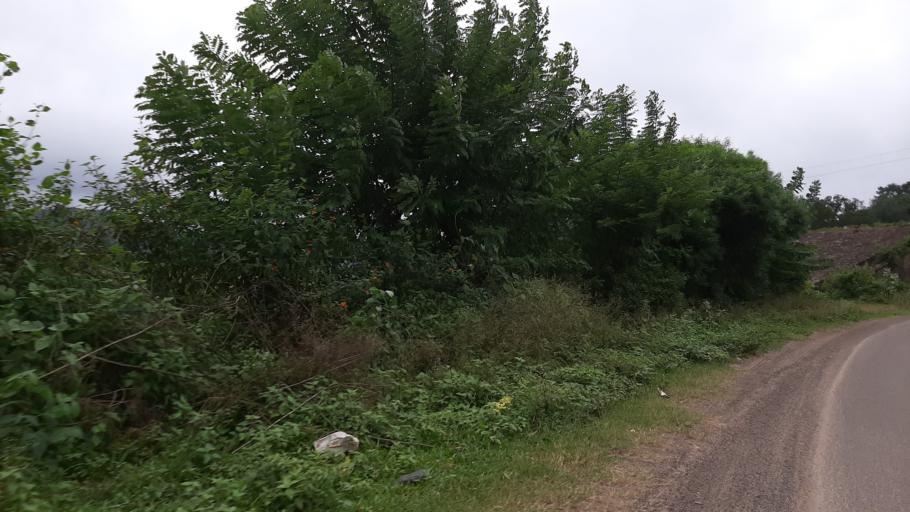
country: IN
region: Andhra Pradesh
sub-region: Vizianagaram District
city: Salur
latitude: 18.3043
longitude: 82.9079
